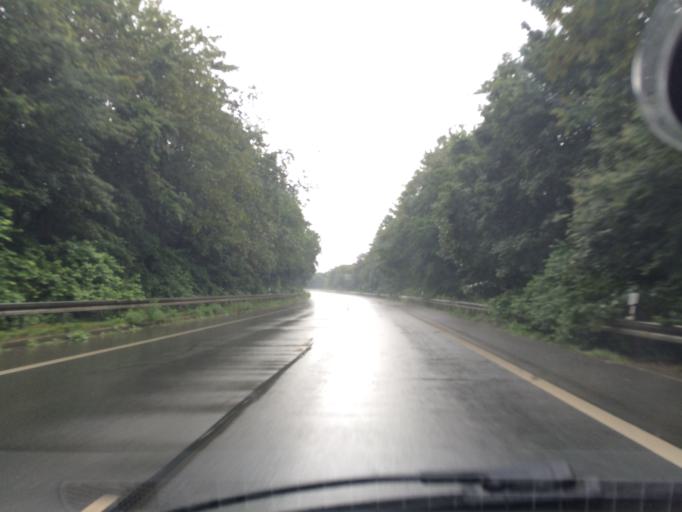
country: DE
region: North Rhine-Westphalia
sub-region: Regierungsbezirk Munster
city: Haltern
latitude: 51.7739
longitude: 7.2338
